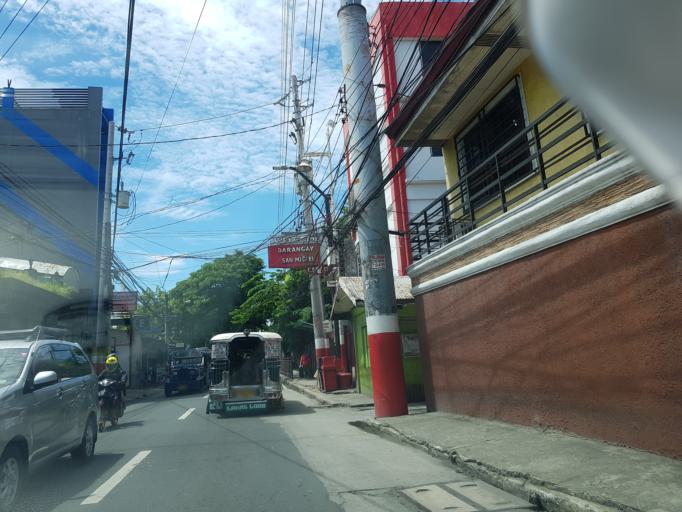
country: PH
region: Calabarzon
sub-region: Province of Rizal
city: Taguig
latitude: 14.5211
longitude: 121.0736
